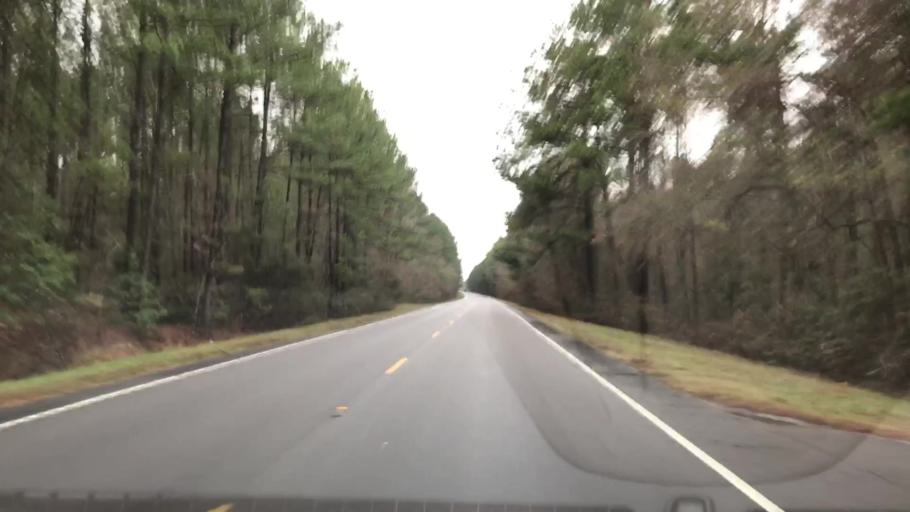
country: US
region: South Carolina
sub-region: Berkeley County
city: Saint Stephen
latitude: 33.2902
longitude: -79.7936
